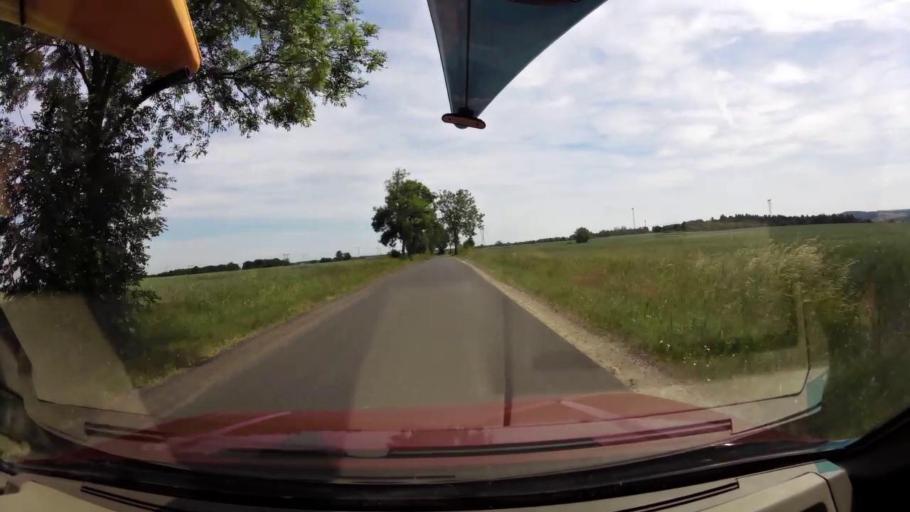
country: PL
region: West Pomeranian Voivodeship
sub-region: Powiat slawienski
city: Darlowo
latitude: 54.3047
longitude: 16.4873
